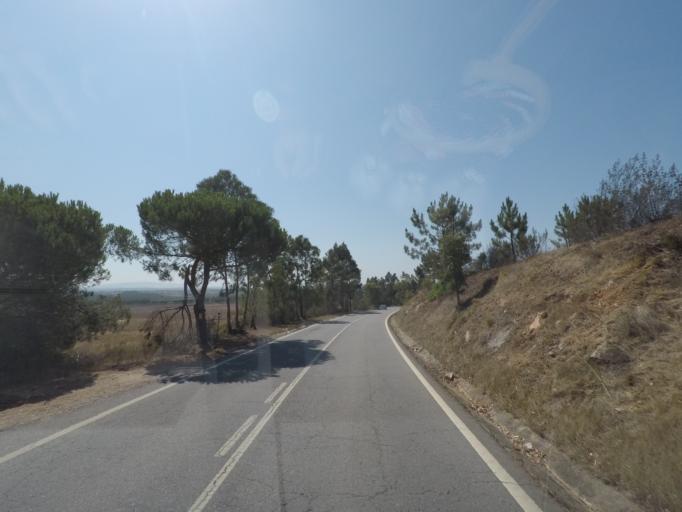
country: PT
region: Beja
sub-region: Odemira
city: Sao Teotonio
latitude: 37.5290
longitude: -8.6994
